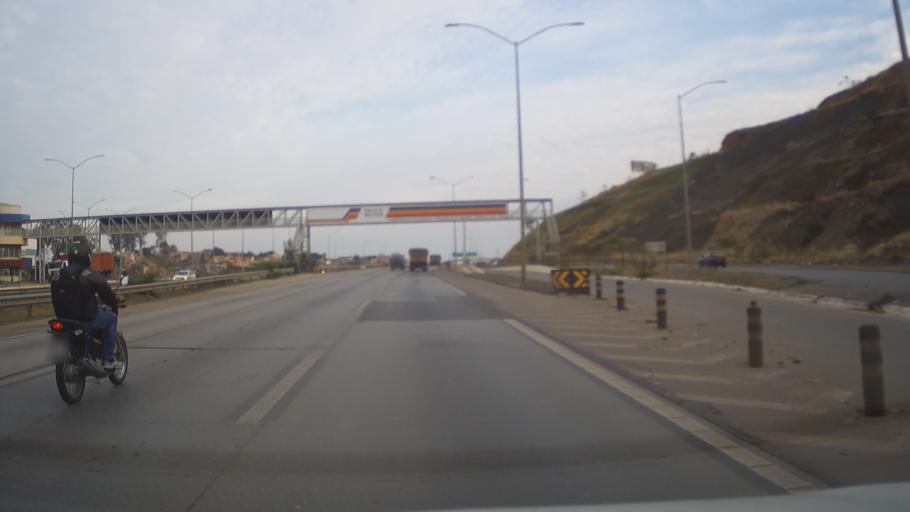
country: BR
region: Minas Gerais
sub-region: Vespasiano
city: Vespasiano
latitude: -19.7776
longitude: -43.9485
